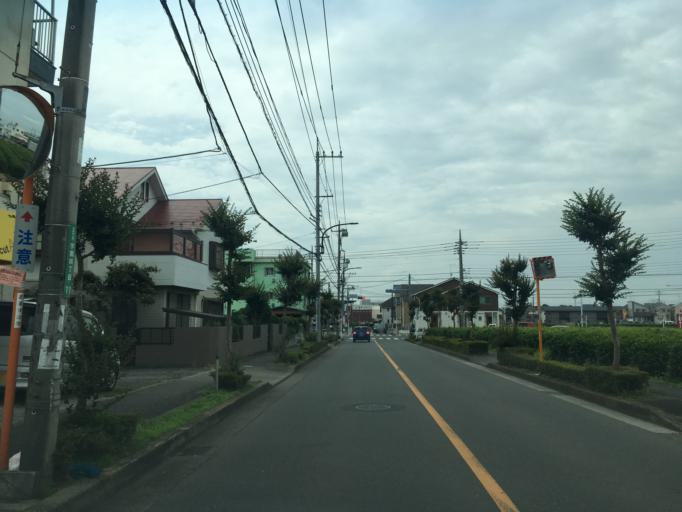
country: JP
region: Tokyo
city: Hino
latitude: 35.7433
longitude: 139.3976
